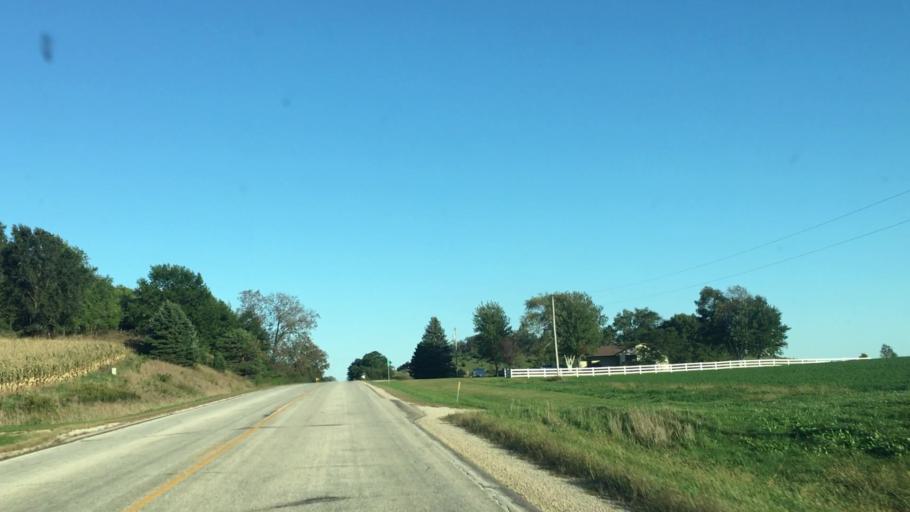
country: US
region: Minnesota
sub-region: Fillmore County
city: Chatfield
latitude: 43.8419
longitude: -92.0876
